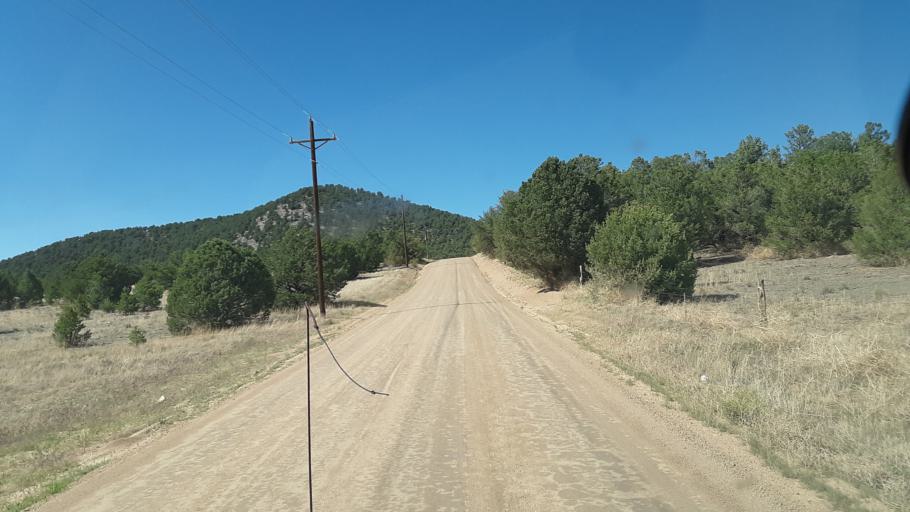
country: US
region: Colorado
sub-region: Custer County
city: Westcliffe
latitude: 38.2938
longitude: -105.4911
